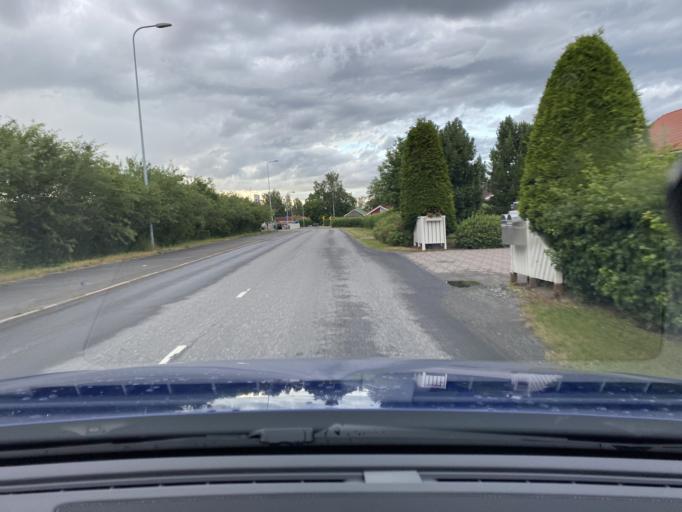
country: FI
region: Satakunta
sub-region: Pori
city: Huittinen
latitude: 61.1718
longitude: 22.6882
